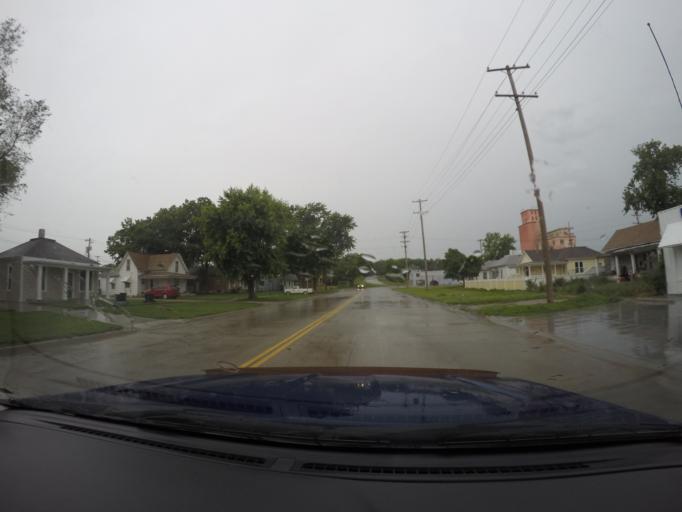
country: US
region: Kansas
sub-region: Cloud County
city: Concordia
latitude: 39.5726
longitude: -97.6638
